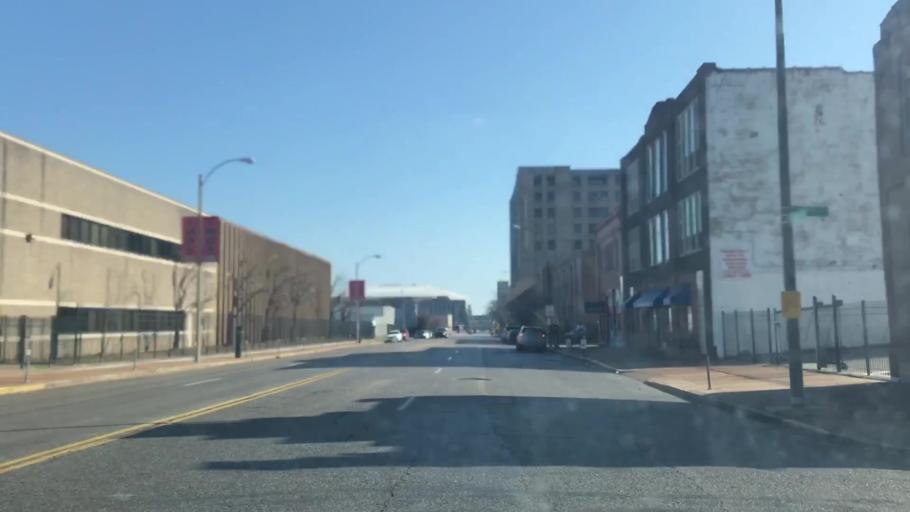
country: US
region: Missouri
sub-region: City of Saint Louis
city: St. Louis
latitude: 38.6346
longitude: -90.2028
